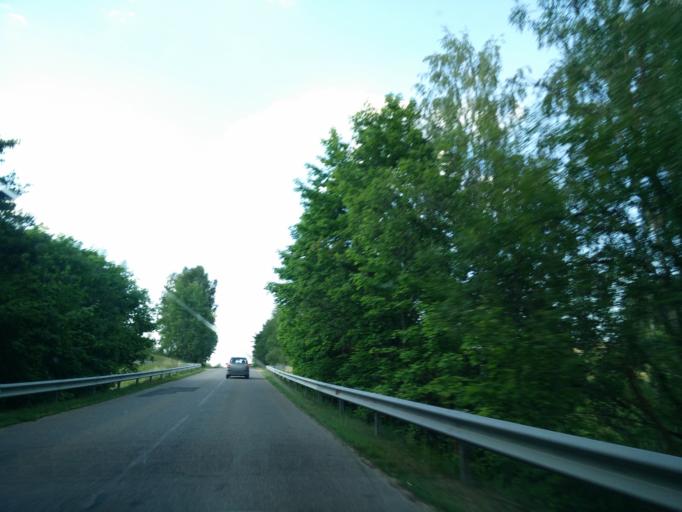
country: LT
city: Trakai
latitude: 54.6811
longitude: 24.9530
